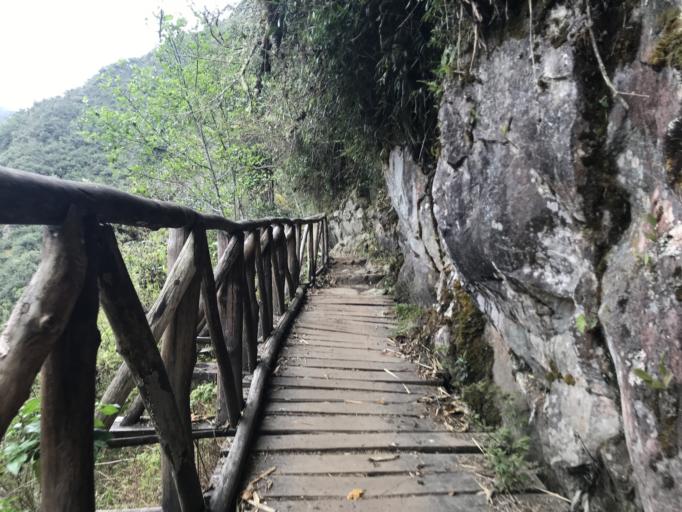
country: PE
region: Cusco
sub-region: Provincia de La Convencion
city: Santa Teresa
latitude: -13.1738
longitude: -72.5348
